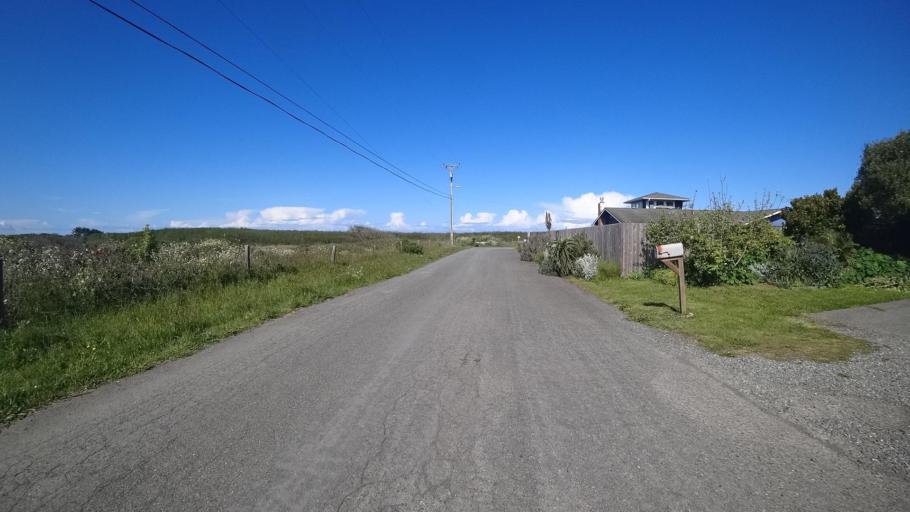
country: US
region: California
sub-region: Humboldt County
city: McKinleyville
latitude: 40.9340
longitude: -124.1268
